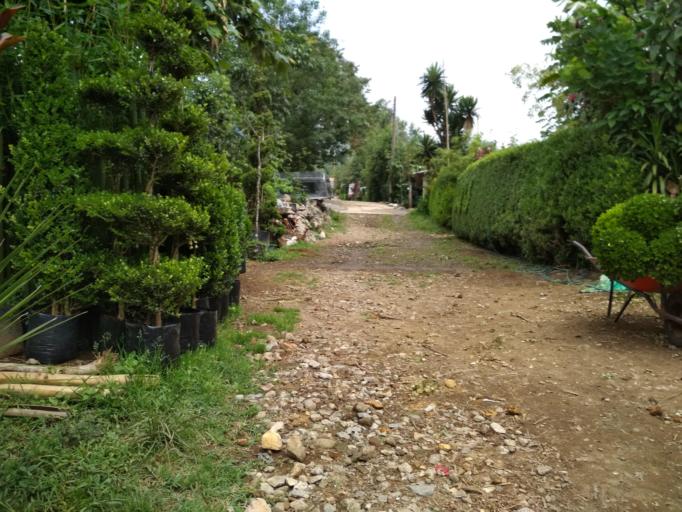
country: MX
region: Veracruz
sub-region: La Perla
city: La Perla
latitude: 18.9264
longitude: -97.1272
